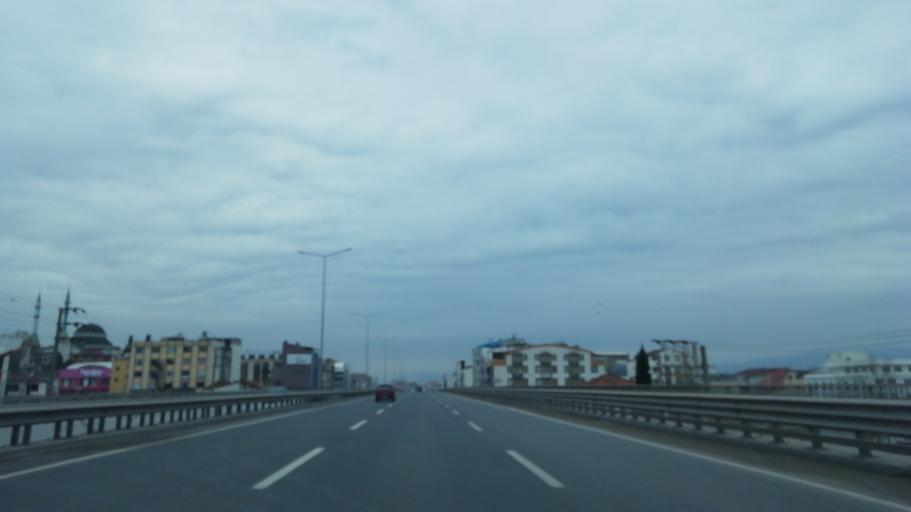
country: TR
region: Kocaeli
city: Korfez
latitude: 40.7623
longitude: 29.7839
